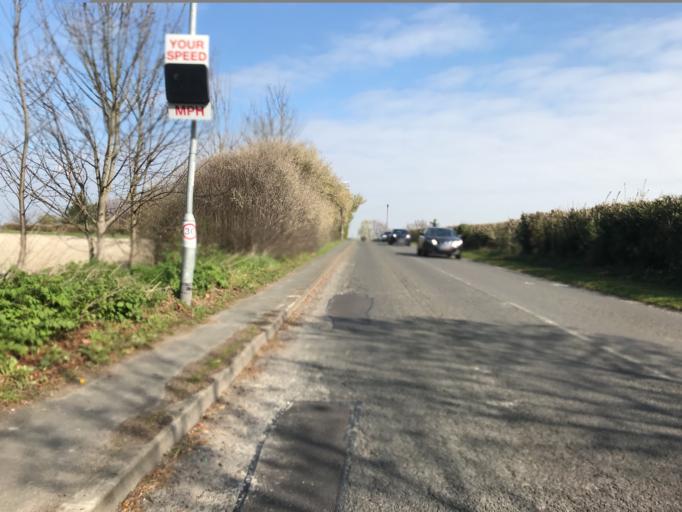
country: GB
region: England
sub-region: Cambridgeshire
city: Sawston
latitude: 52.1586
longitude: 0.1552
